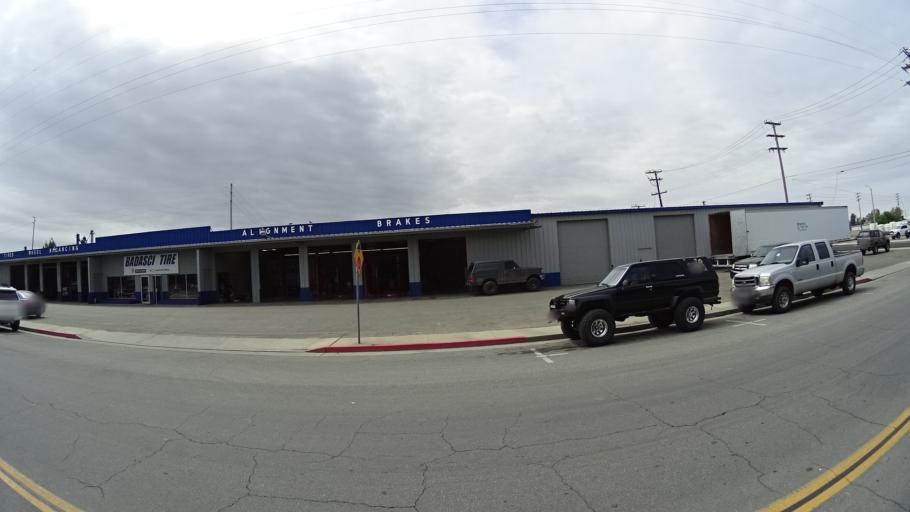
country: US
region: California
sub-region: Kings County
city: Hanford
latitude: 36.3249
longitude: -119.6497
